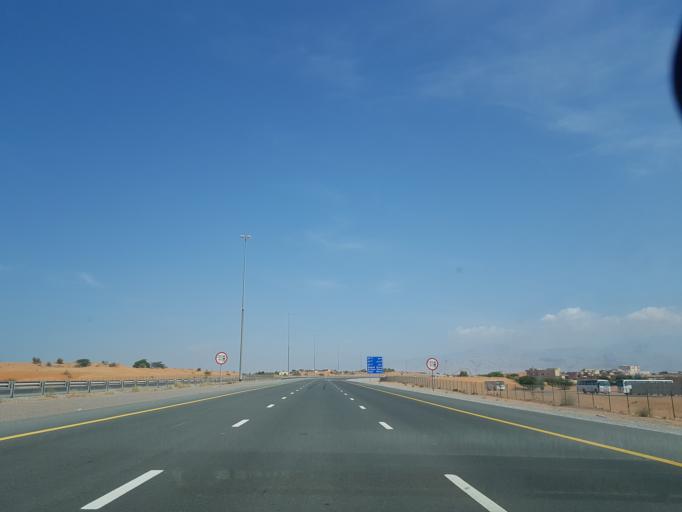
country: AE
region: Ra's al Khaymah
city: Ras al-Khaimah
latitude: 25.7016
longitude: 55.9340
